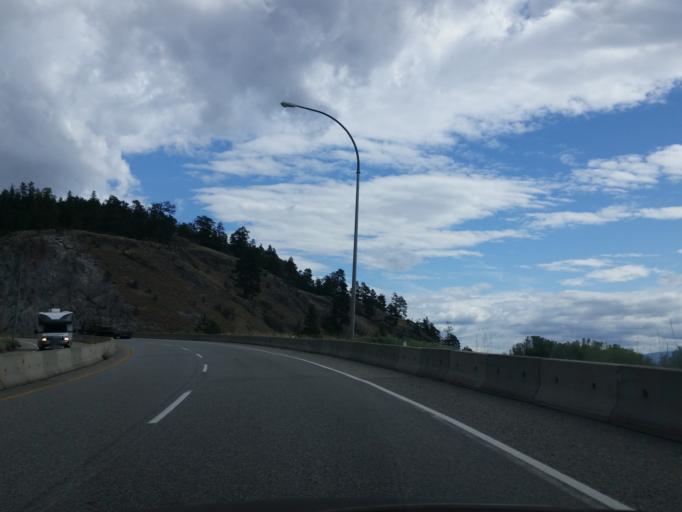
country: CA
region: British Columbia
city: Peachland
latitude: 49.8047
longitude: -119.6633
